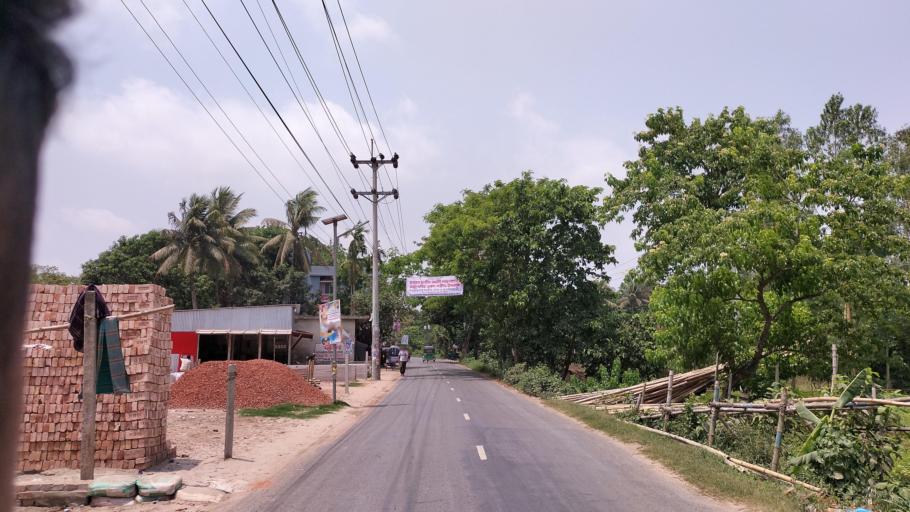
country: BD
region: Dhaka
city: Azimpur
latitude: 23.7296
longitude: 90.2870
